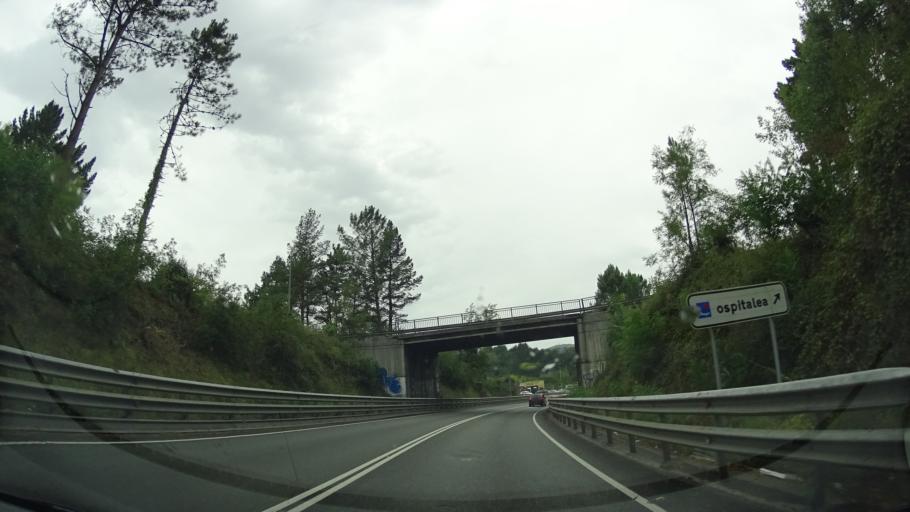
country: ES
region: Basque Country
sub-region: Bizkaia
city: Galdakao
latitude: 43.2226
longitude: -2.8192
